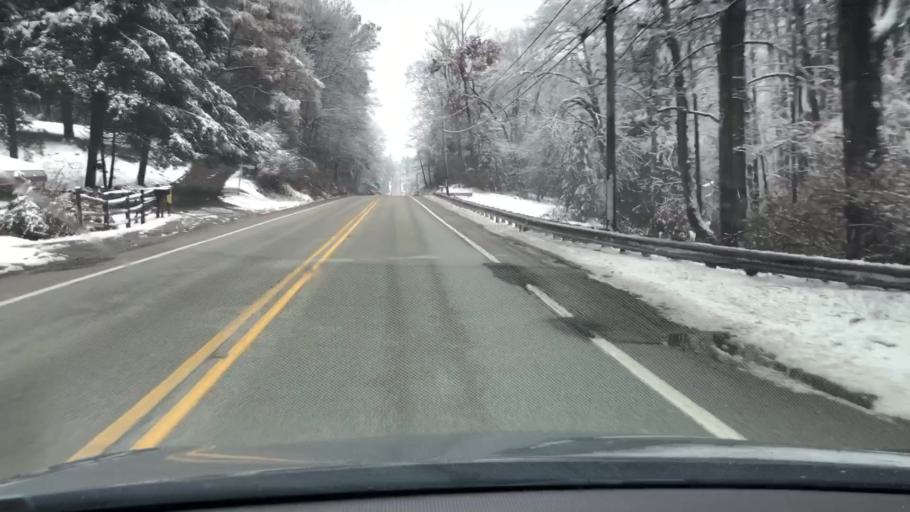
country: US
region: Pennsylvania
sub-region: Fayette County
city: Hopwood
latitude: 39.8282
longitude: -79.5972
